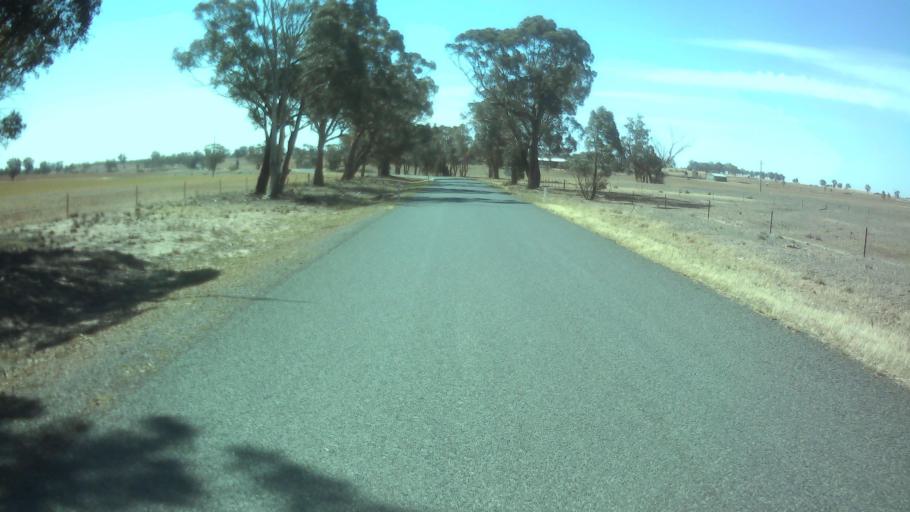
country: AU
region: New South Wales
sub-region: Weddin
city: Grenfell
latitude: -33.7654
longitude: 147.8645
